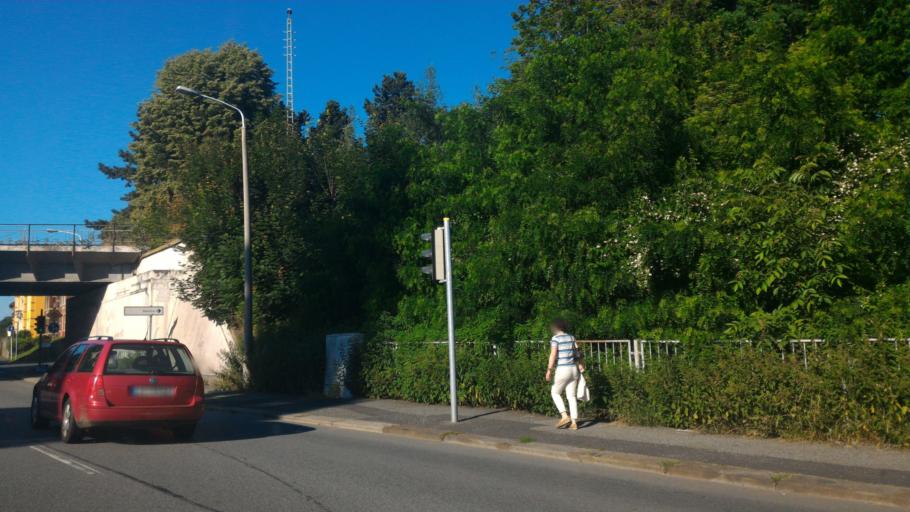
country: DE
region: Saxony
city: Zittau
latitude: 50.9038
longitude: 14.8125
